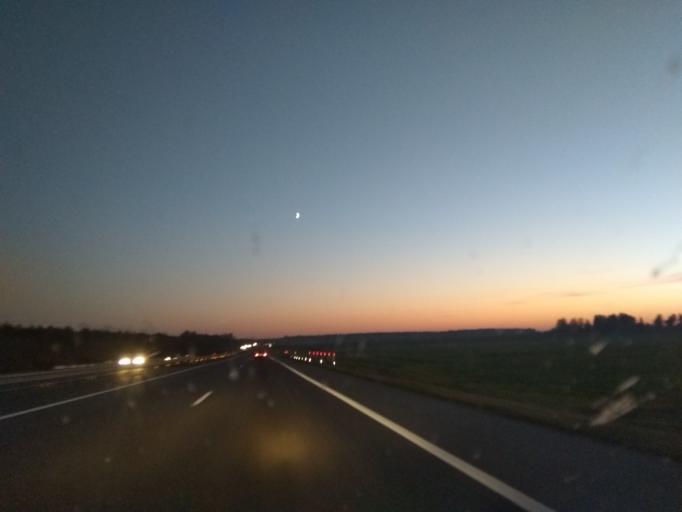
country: BY
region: Minsk
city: Enyerhyetykaw
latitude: 53.6148
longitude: 27.0499
